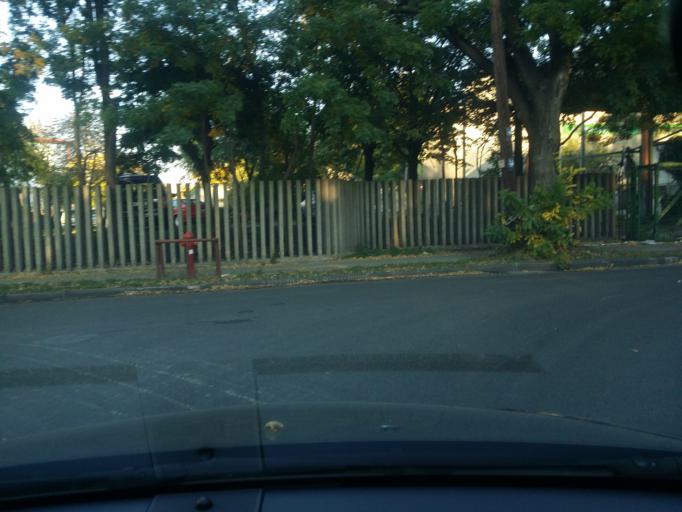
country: HU
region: Budapest
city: Budapest XIII. keruelet
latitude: 47.5234
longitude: 19.0783
